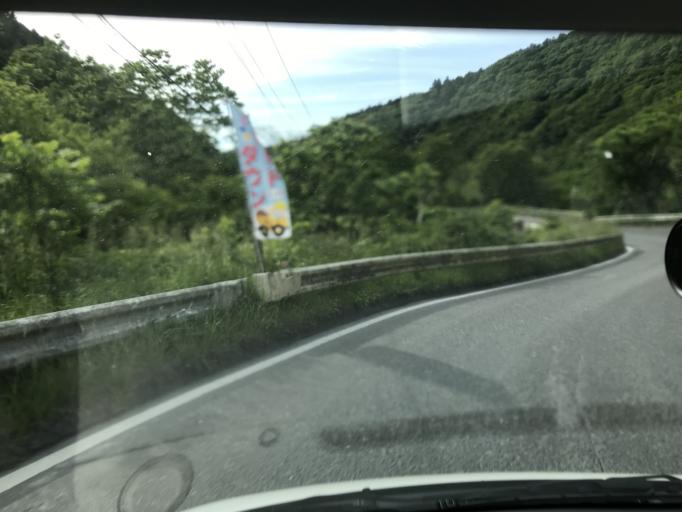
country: JP
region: Miyagi
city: Wakuya
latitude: 38.6577
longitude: 141.3156
